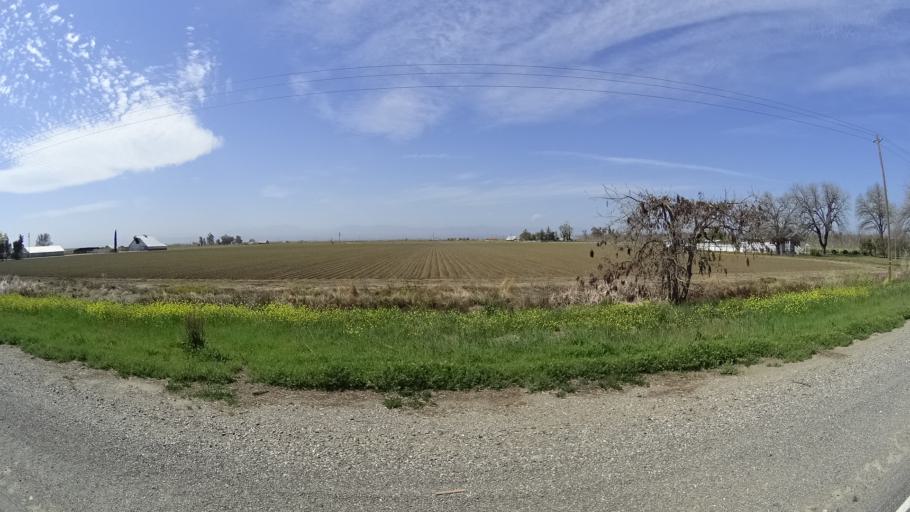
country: US
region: California
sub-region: Glenn County
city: Willows
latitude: 39.5723
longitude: -122.1936
